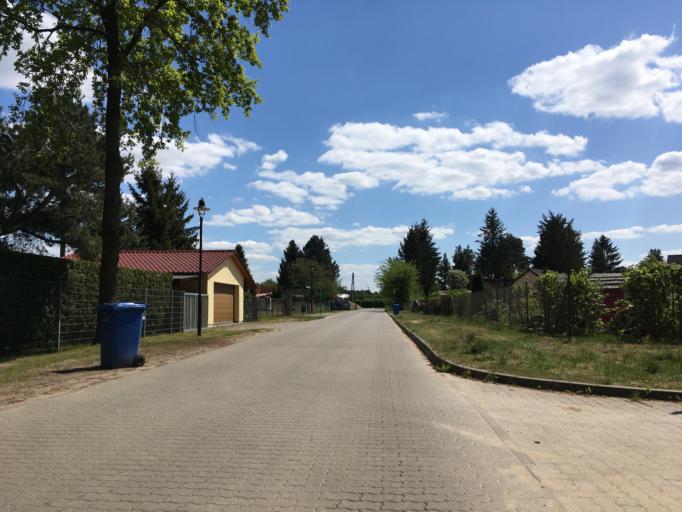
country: DE
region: Brandenburg
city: Biesenthal
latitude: 52.7440
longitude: 13.6526
